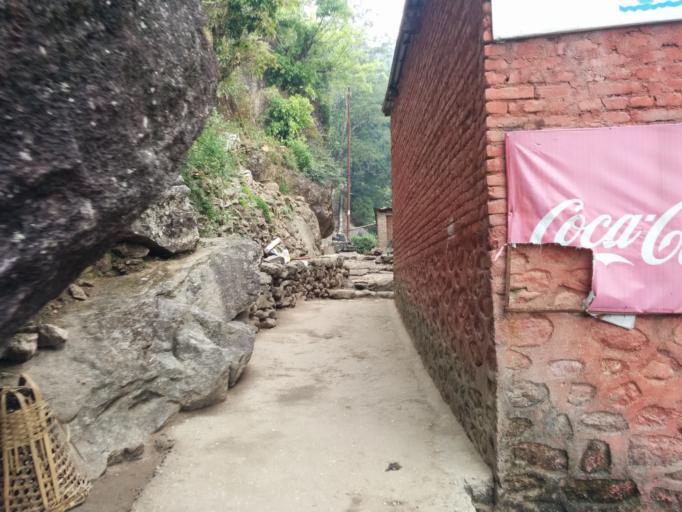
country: NP
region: Central Region
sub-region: Bagmati Zone
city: Bhaktapur
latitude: 27.7656
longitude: 85.4238
